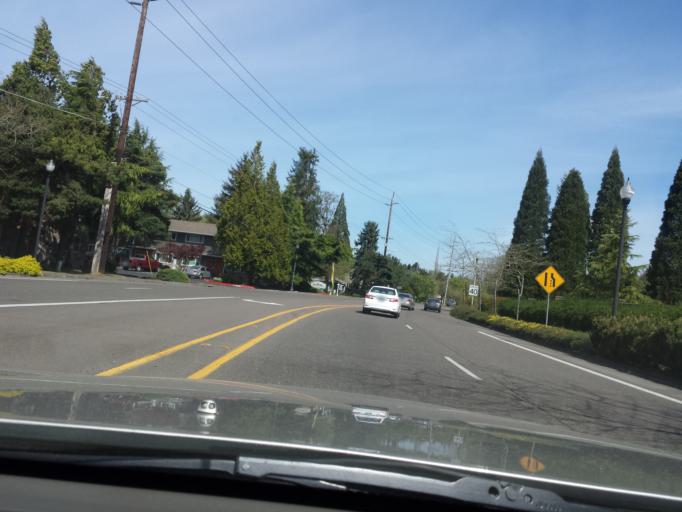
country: US
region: Oregon
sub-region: Washington County
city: Aloha
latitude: 45.4941
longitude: -122.8524
